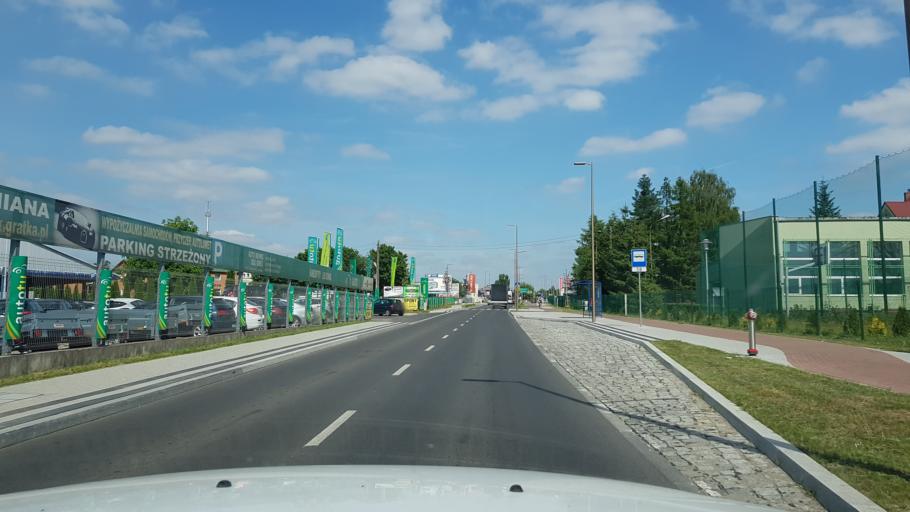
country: PL
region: West Pomeranian Voivodeship
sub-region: Powiat goleniowski
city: Goleniow
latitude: 53.5609
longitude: 14.8430
